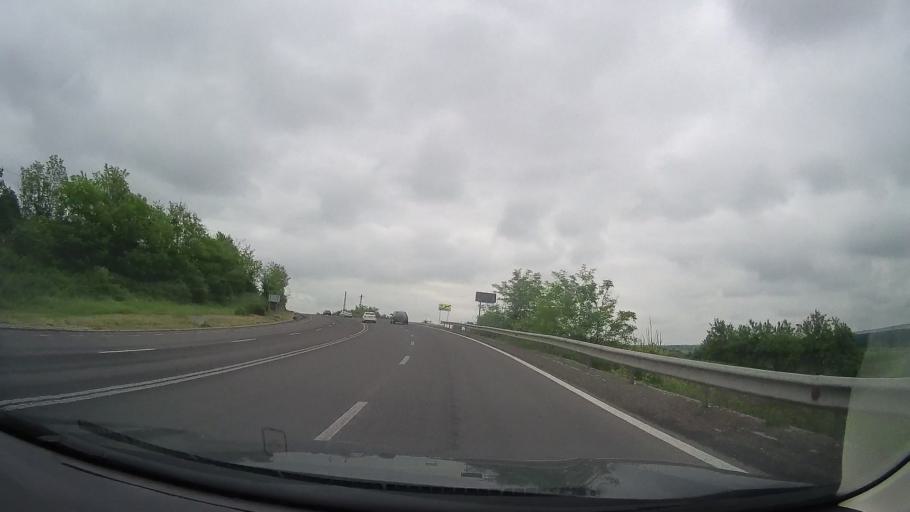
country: RO
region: Dolj
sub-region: Comuna Scaesti
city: Scaesti
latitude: 44.5014
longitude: 23.5975
